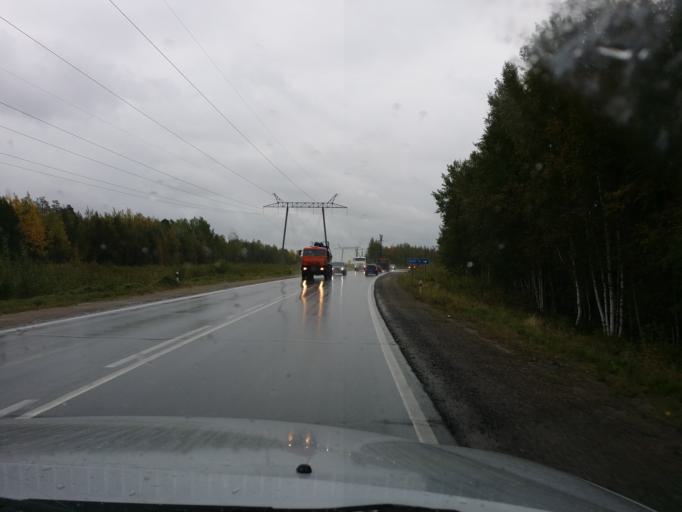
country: RU
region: Khanty-Mansiyskiy Avtonomnyy Okrug
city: Megion
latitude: 61.1600
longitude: 75.7249
